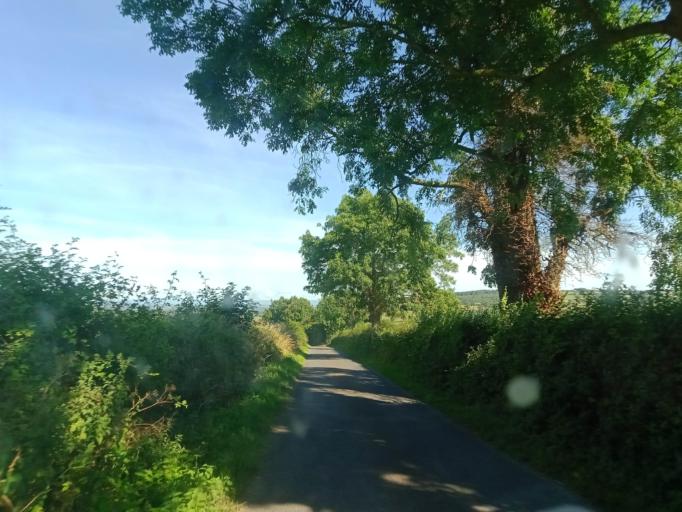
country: IE
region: Leinster
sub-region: Kilkenny
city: Ballyragget
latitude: 52.7980
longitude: -7.4257
